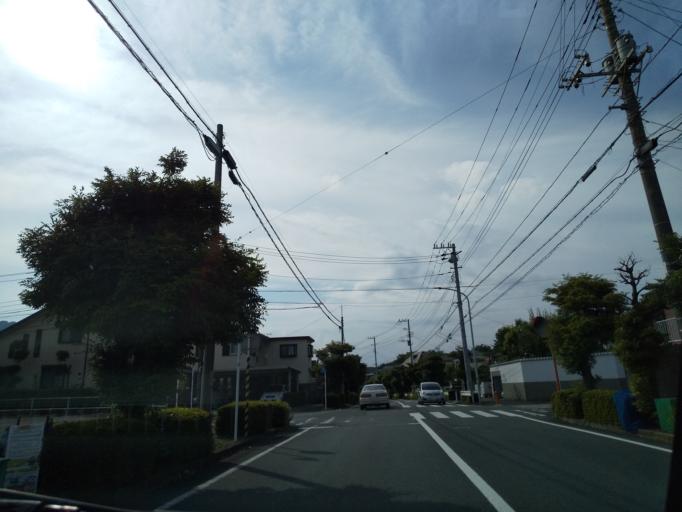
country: JP
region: Kanagawa
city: Zama
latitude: 35.4936
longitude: 139.3243
